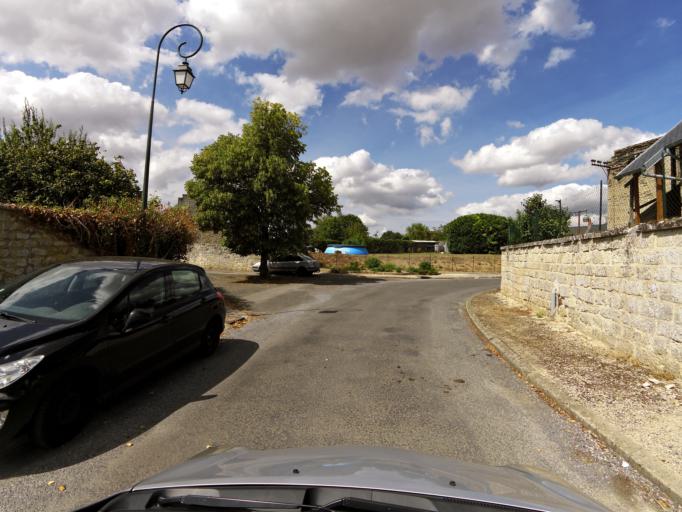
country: FR
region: Picardie
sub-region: Departement de l'Aisne
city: Courmelles
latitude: 49.3186
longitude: 3.2644
